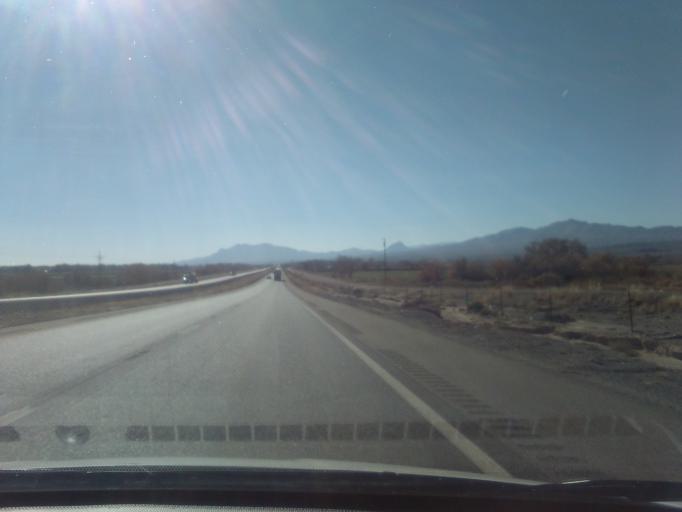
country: US
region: New Mexico
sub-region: Socorro County
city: Socorro
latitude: 34.2691
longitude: -106.9033
